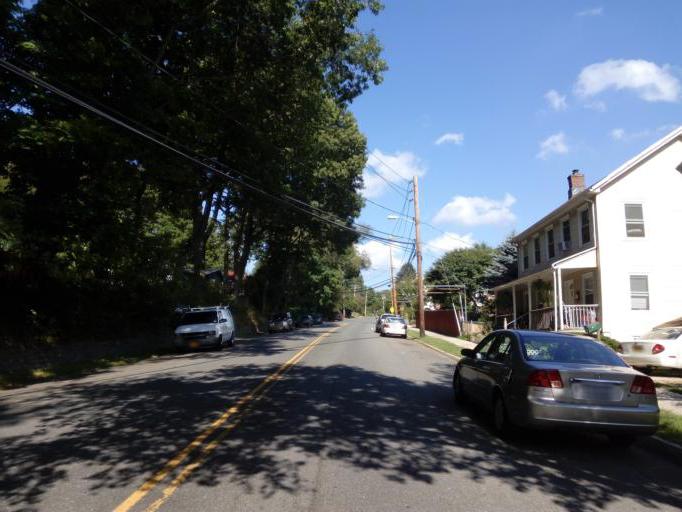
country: US
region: New York
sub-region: Nassau County
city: Glen Cove
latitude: 40.8660
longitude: -73.6489
